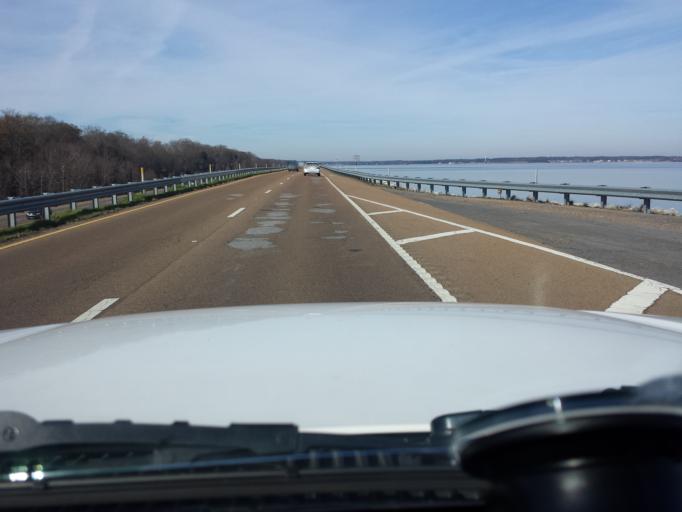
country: US
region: Mississippi
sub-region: Madison County
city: Ridgeland
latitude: 32.3882
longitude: -90.0502
